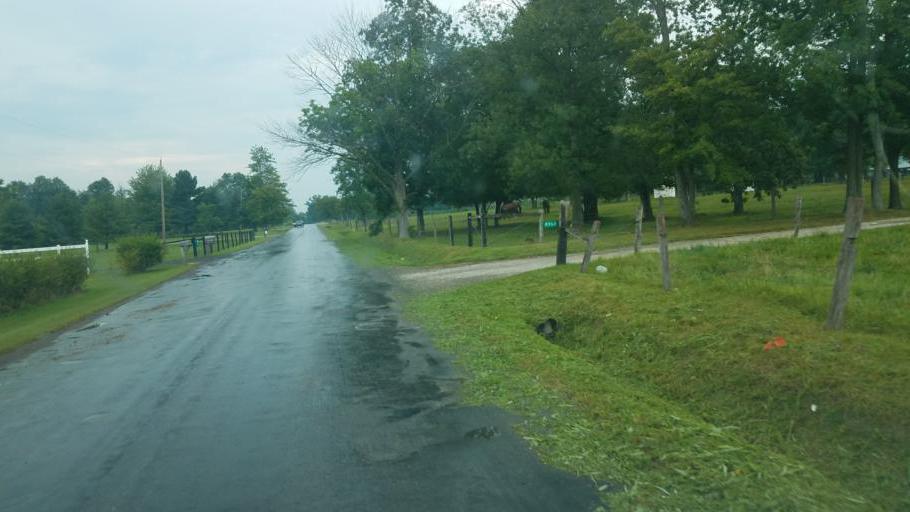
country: US
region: Ohio
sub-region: Geauga County
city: Middlefield
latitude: 41.4650
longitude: -80.9748
